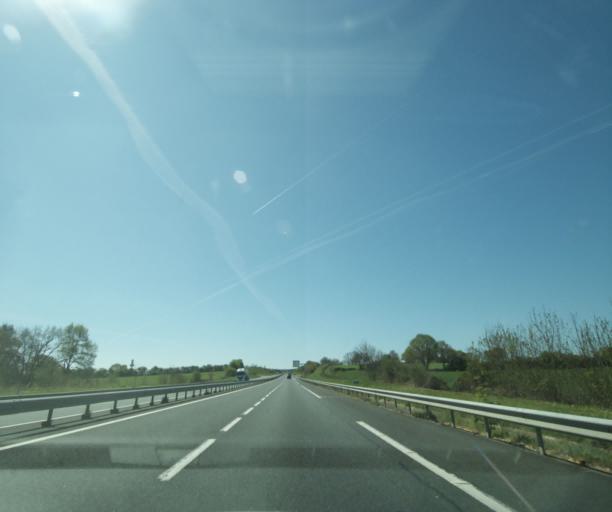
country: FR
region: Centre
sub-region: Departement de l'Indre
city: Le Pechereau
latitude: 46.5129
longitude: 1.5092
